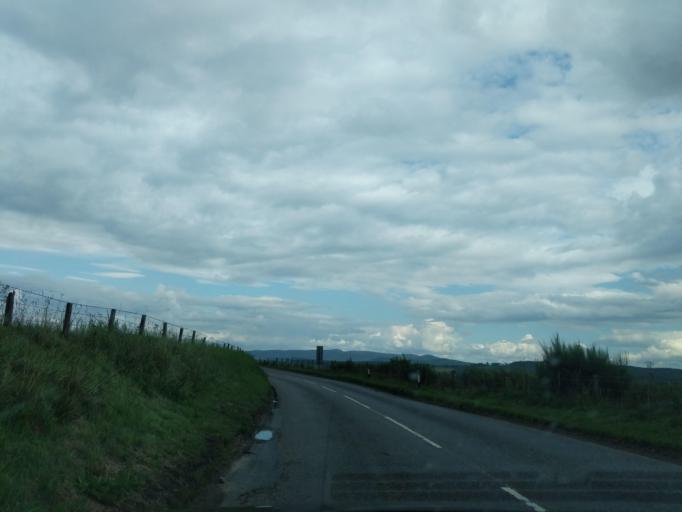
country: GB
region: Scotland
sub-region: Highland
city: Aviemore
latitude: 57.2967
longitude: -3.7661
